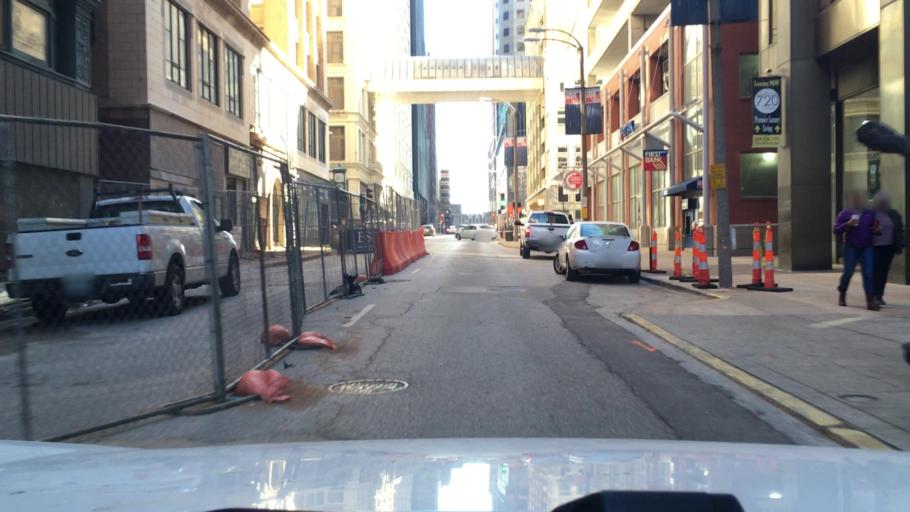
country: US
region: Missouri
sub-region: City of Saint Louis
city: St. Louis
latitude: 38.6286
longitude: -90.1922
